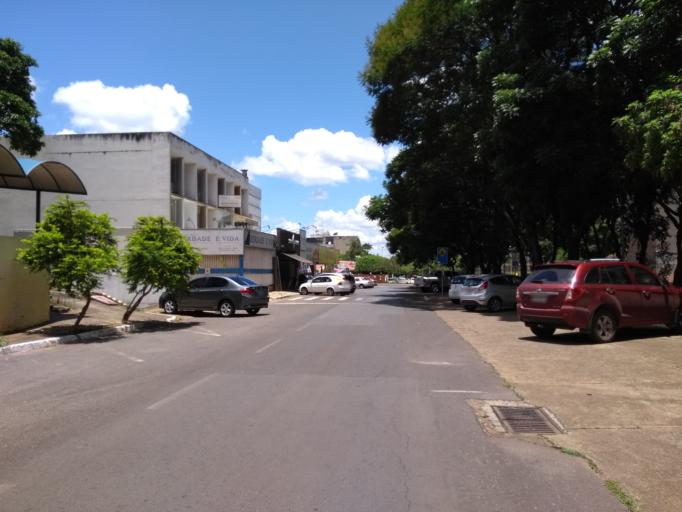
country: BR
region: Federal District
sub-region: Brasilia
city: Brasilia
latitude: -15.7702
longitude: -47.8885
